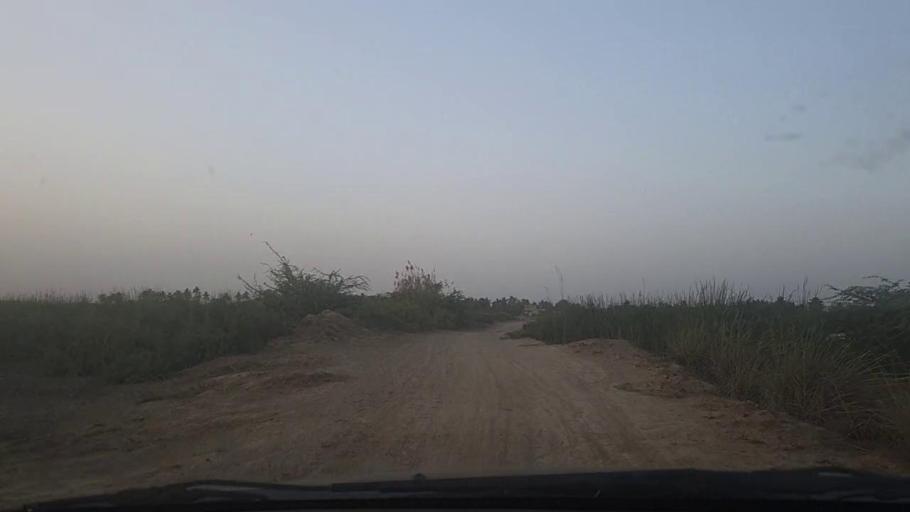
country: PK
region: Sindh
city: Mirpur Sakro
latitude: 24.3780
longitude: 67.6571
